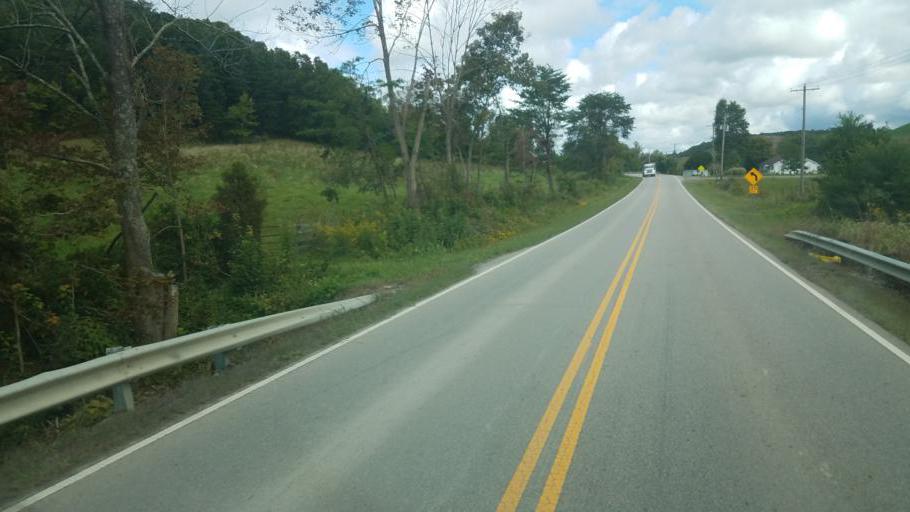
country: US
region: Ohio
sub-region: Scioto County
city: Lucasville
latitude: 38.8596
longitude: -82.9050
